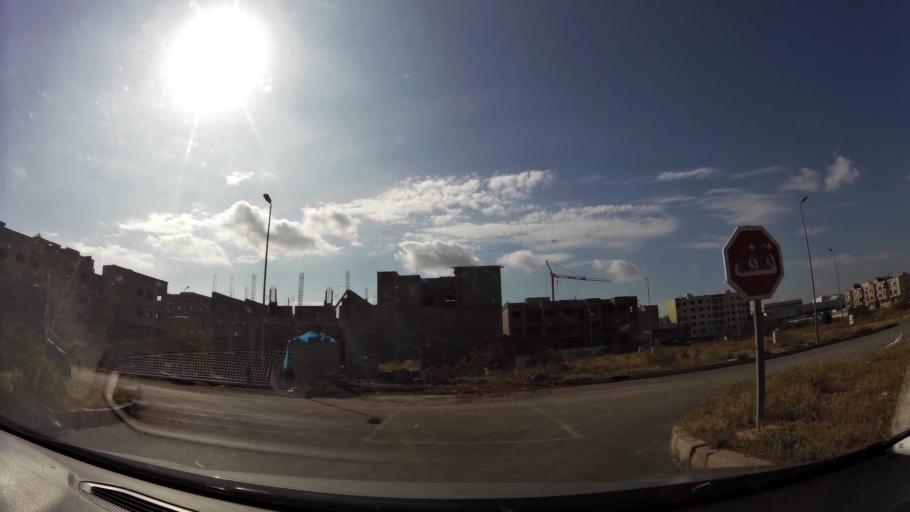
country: MA
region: Rabat-Sale-Zemmour-Zaer
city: Sale
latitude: 34.0589
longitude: -6.8095
